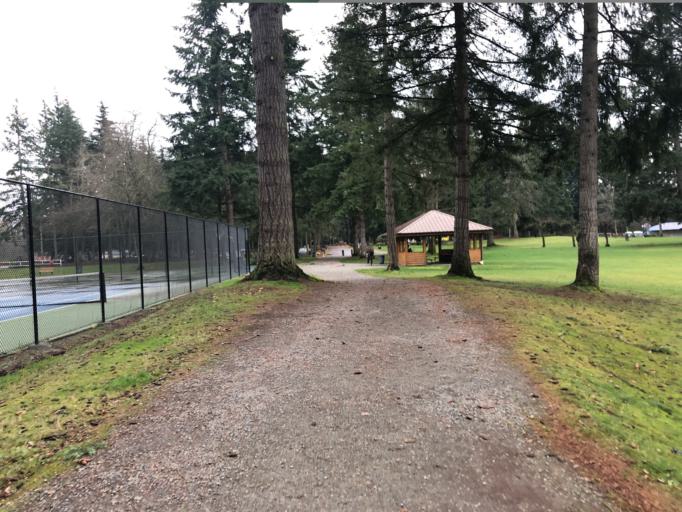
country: US
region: Washington
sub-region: King County
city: Lakeland South
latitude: 47.2744
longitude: -122.2803
